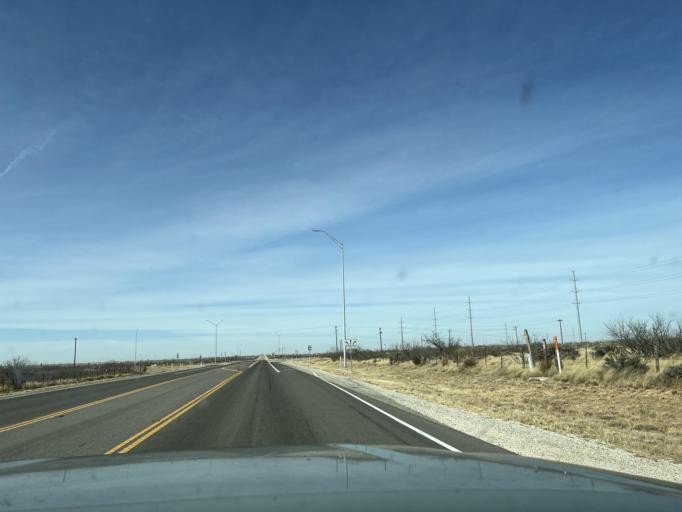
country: US
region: Texas
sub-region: Andrews County
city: Andrews
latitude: 32.3569
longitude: -102.7698
